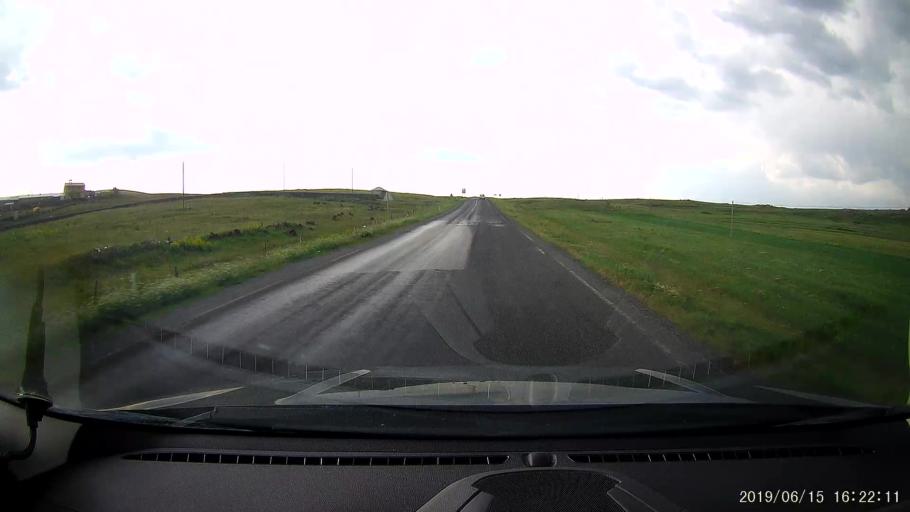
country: TR
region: Ardahan
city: Hanak
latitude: 41.1906
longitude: 42.8478
